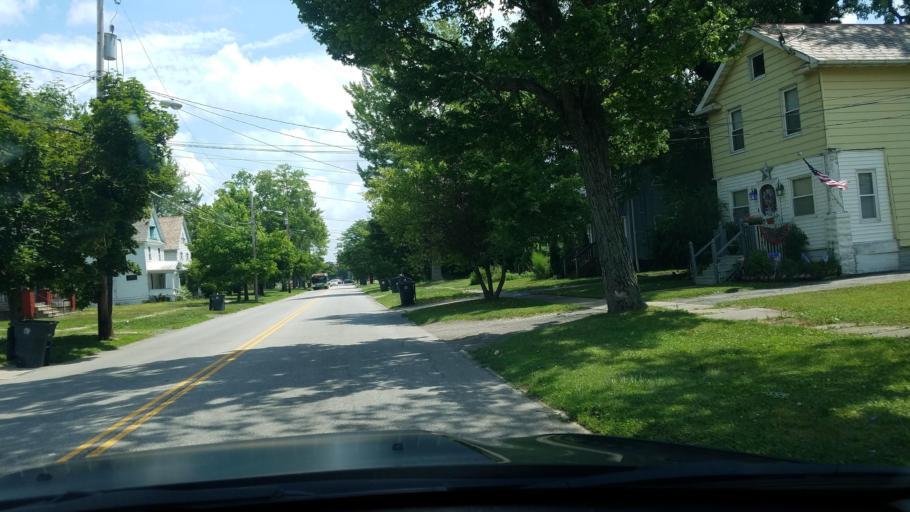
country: US
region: Ohio
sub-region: Trumbull County
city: Warren
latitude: 41.2450
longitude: -80.8210
